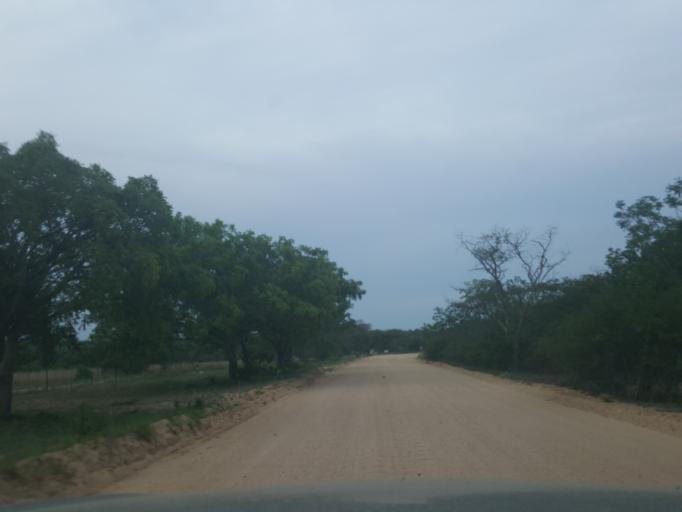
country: ZA
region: Limpopo
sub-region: Mopani District Municipality
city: Hoedspruit
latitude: -24.5438
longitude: 31.0253
